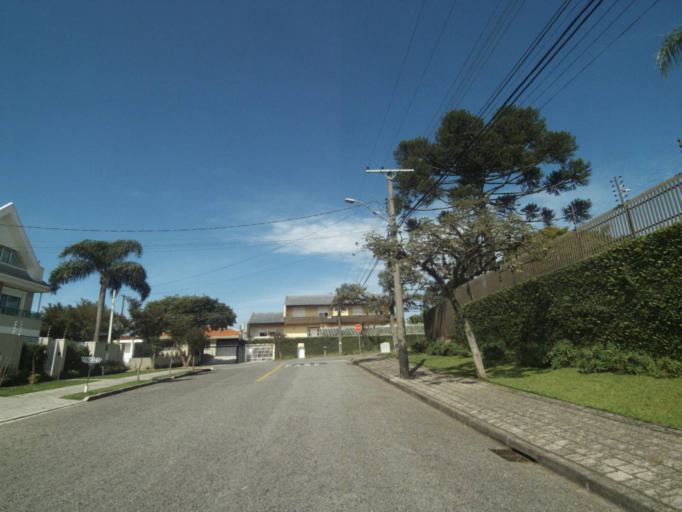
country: BR
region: Parana
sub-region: Curitiba
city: Curitiba
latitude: -25.4580
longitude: -49.2441
